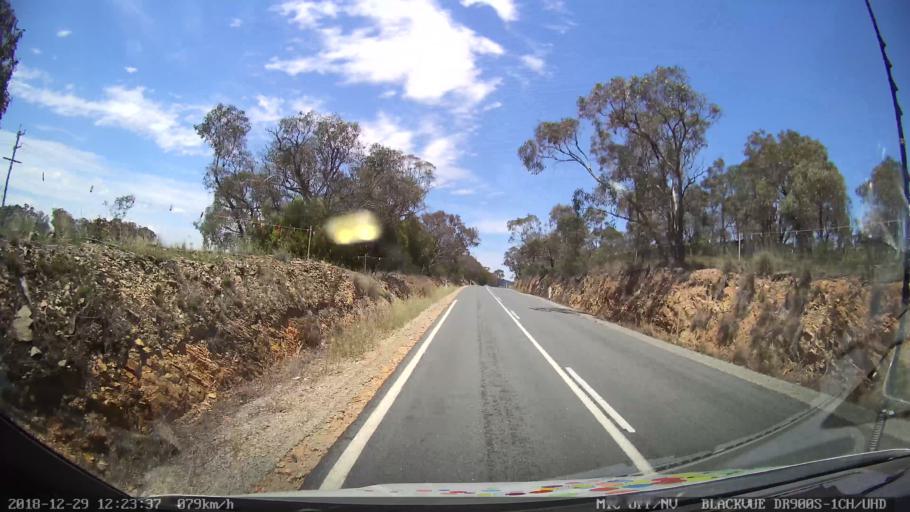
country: AU
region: New South Wales
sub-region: Queanbeyan
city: Queanbeyan
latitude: -35.4385
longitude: 149.2160
